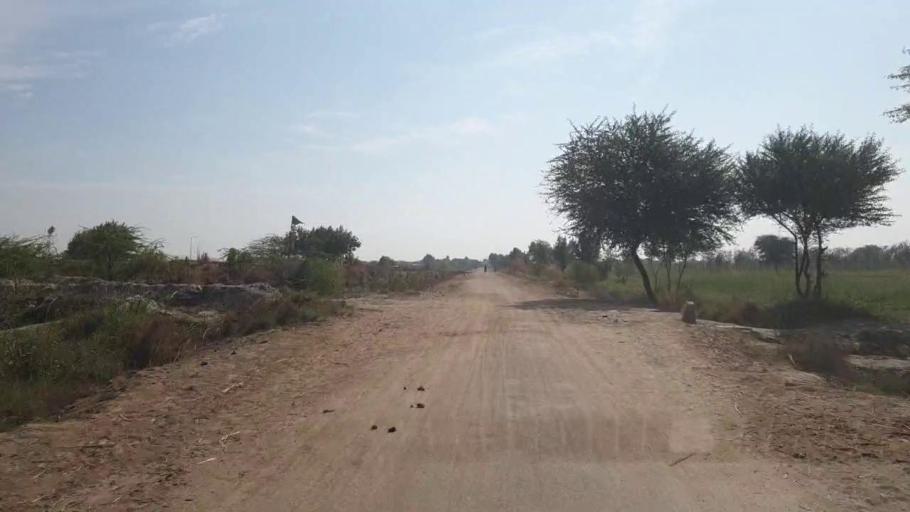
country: PK
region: Sindh
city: Mirwah Gorchani
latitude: 25.3638
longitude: 69.1968
